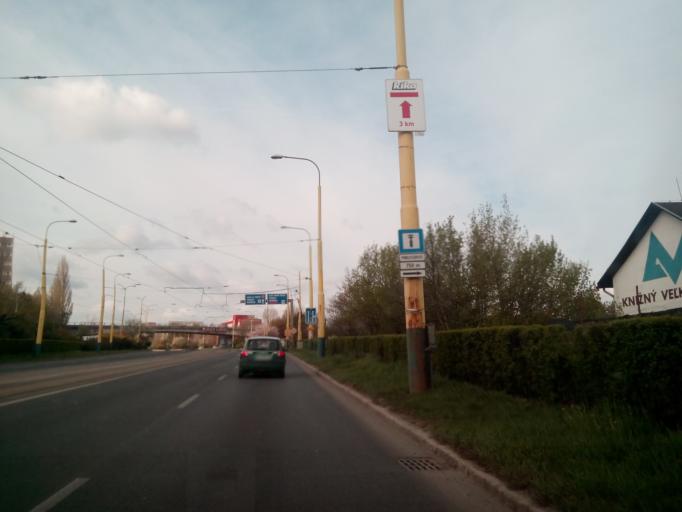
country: SK
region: Kosicky
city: Kosice
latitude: 48.7260
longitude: 21.2384
